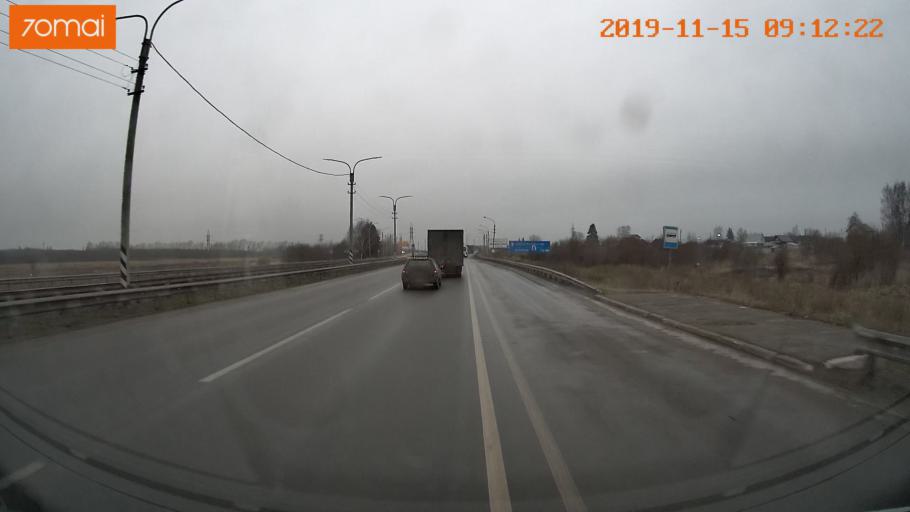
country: RU
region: Vologda
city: Tonshalovo
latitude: 59.2072
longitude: 37.9378
